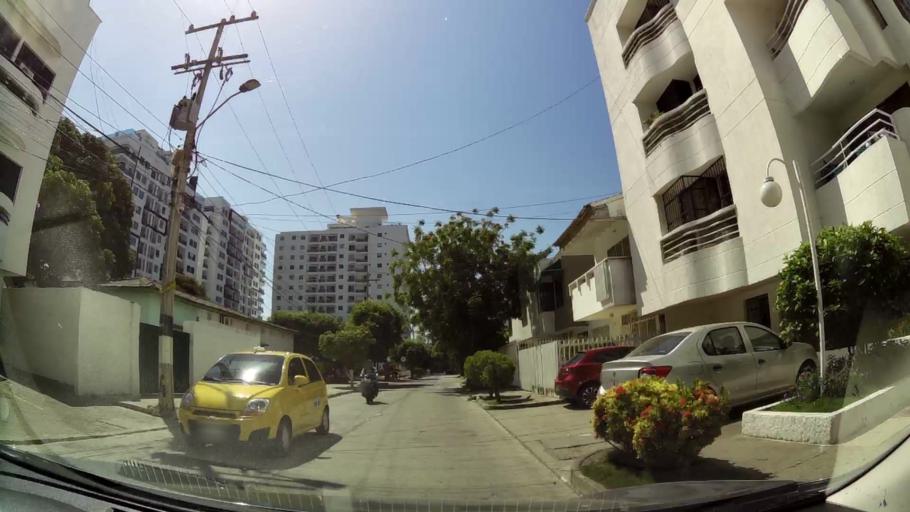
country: CO
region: Bolivar
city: Cartagena
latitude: 10.4443
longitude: -75.5216
